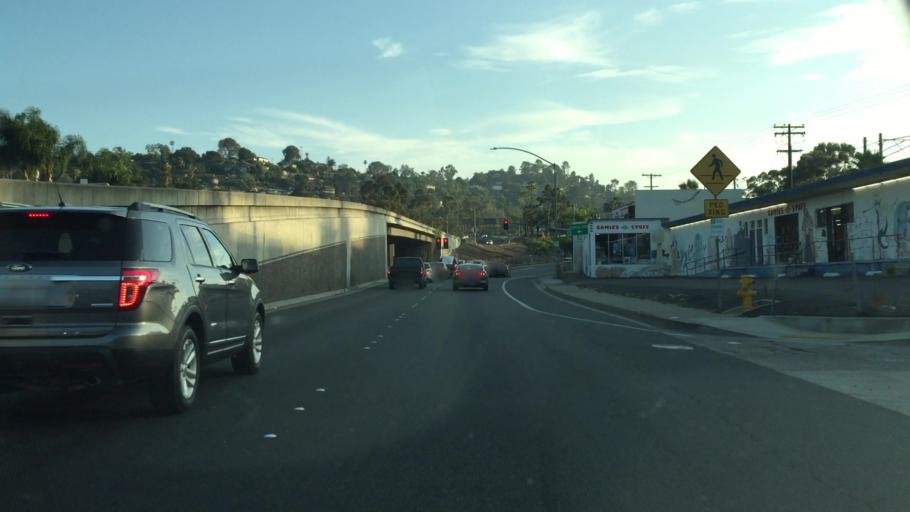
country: US
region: California
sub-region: San Diego County
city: El Cajon
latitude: 32.7840
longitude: -116.9786
